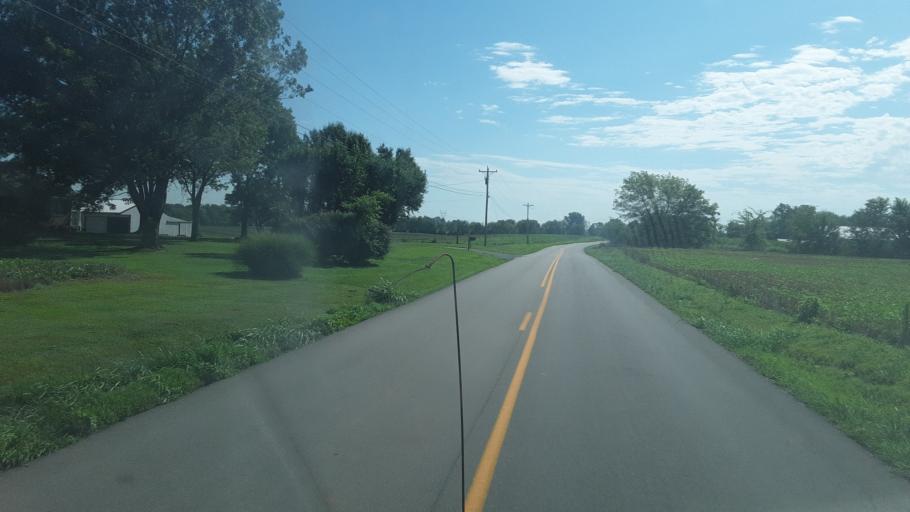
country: US
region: Kentucky
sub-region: Todd County
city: Elkton
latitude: 36.7382
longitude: -87.2438
